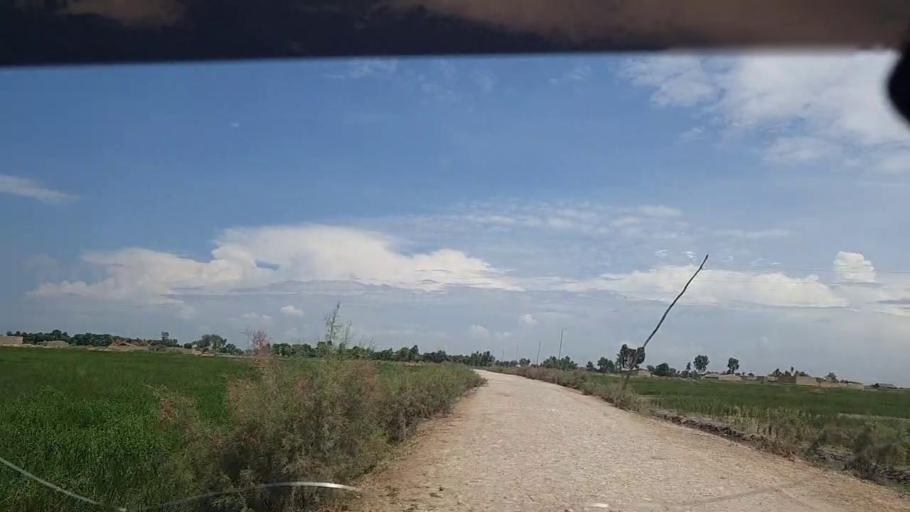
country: PK
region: Sindh
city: Ghauspur
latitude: 28.1506
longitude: 68.9484
